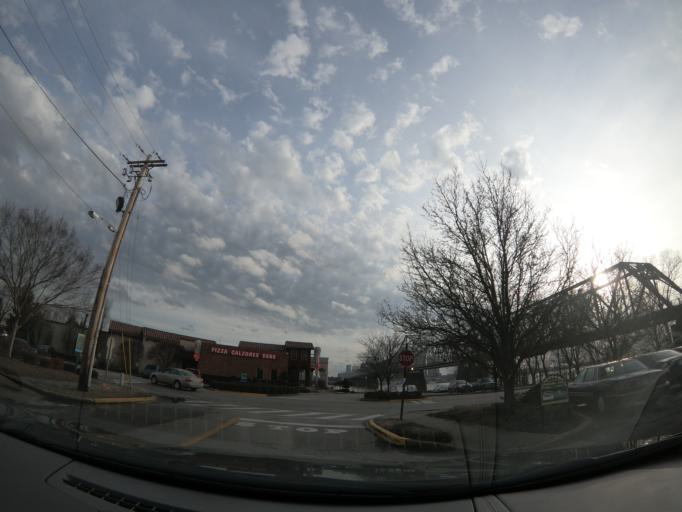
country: US
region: Indiana
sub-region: Clark County
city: Jeffersonville
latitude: 38.2688
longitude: -85.7495
